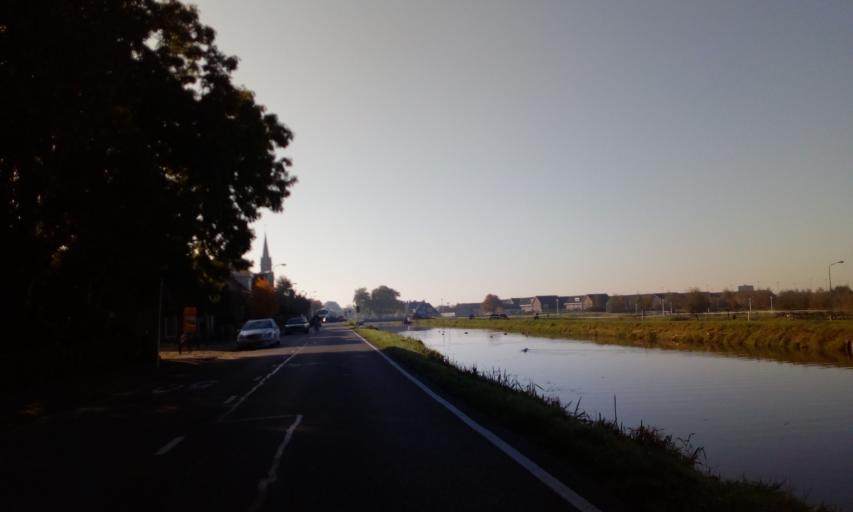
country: NL
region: South Holland
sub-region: Gemeente Lansingerland
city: Berkel en Rodenrijs
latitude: 52.0035
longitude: 4.4826
